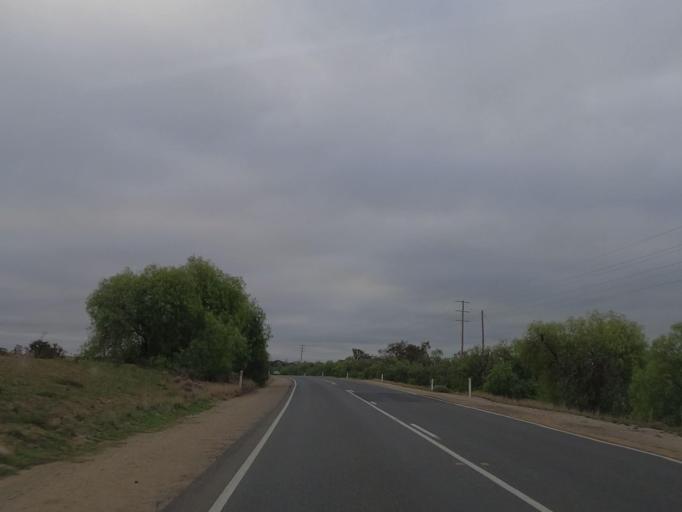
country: AU
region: Victoria
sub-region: Swan Hill
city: Swan Hill
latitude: -35.4462
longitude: 143.6204
